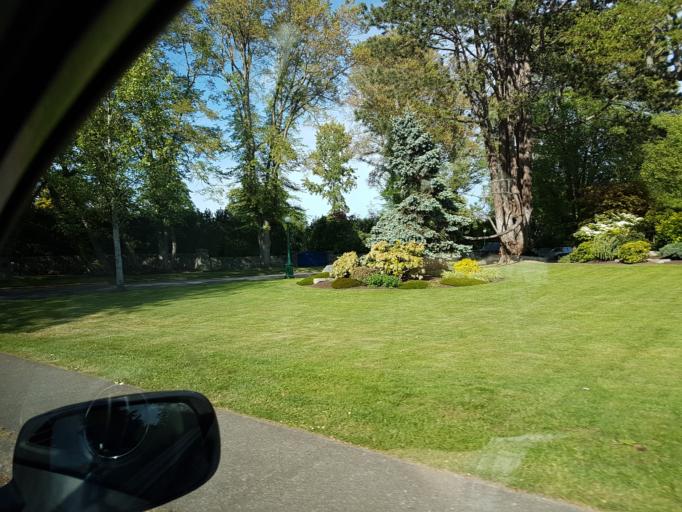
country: CA
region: British Columbia
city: Oak Bay
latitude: 48.4432
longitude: -123.2934
